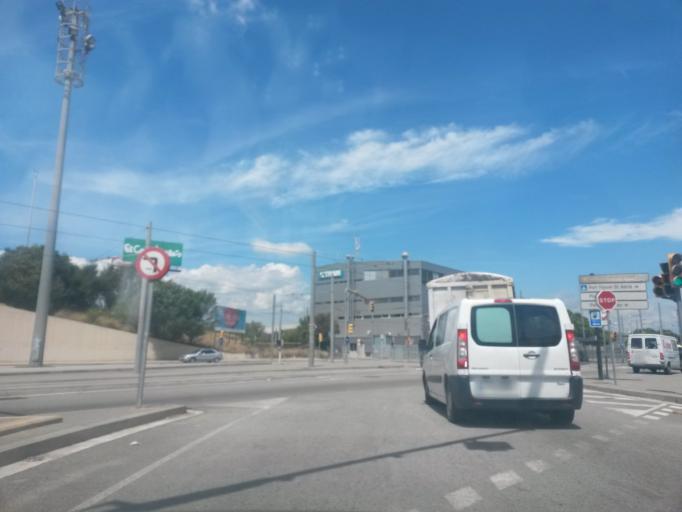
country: ES
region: Catalonia
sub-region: Provincia de Barcelona
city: Sant Adria de Besos
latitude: 41.4182
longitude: 2.2258
